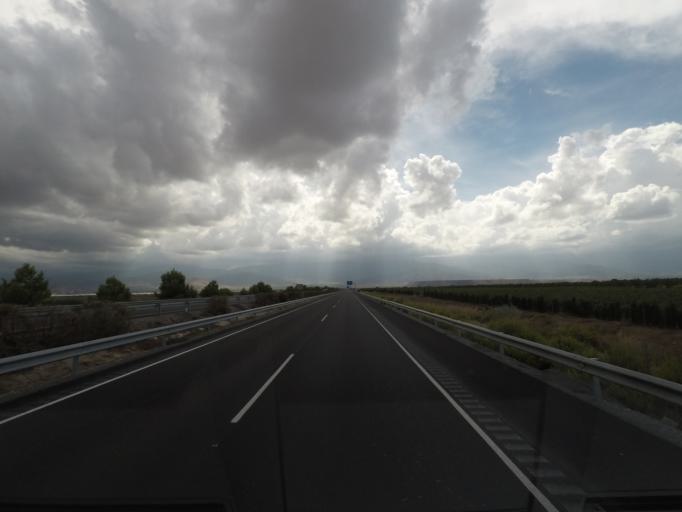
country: ES
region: Andalusia
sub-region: Provincia de Granada
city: Albunan
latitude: 37.2424
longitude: -3.0820
